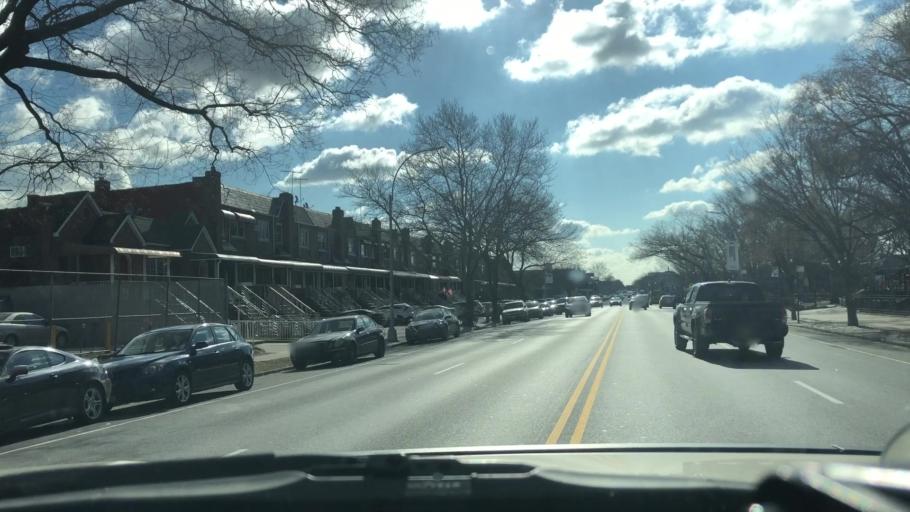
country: US
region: New York
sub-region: Kings County
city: Bensonhurst
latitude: 40.6138
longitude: -74.0135
